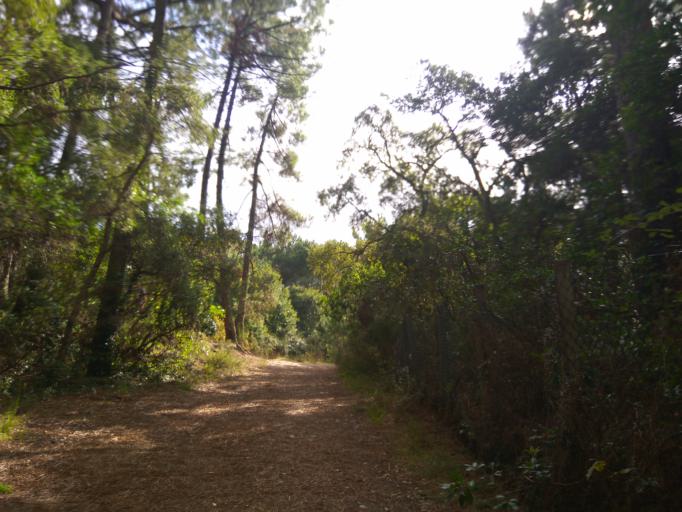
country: FR
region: Aquitaine
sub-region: Departement des Landes
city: Capbreton
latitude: 43.6297
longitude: -1.4430
